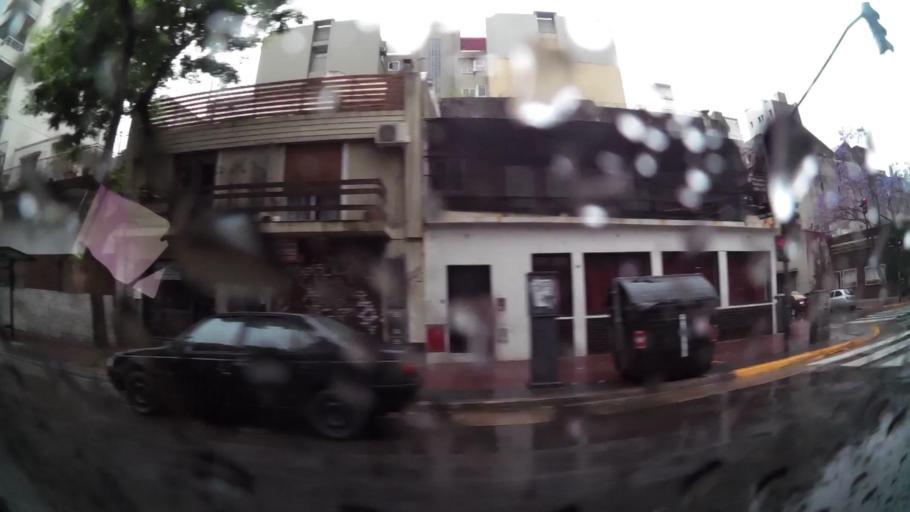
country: AR
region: Buenos Aires F.D.
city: Buenos Aires
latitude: -34.6244
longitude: -58.3743
